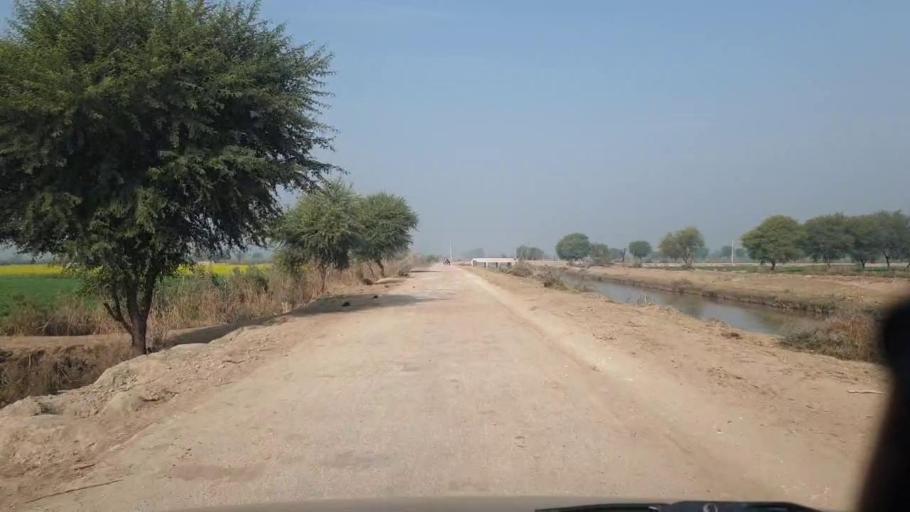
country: PK
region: Sindh
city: Shahdadpur
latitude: 26.0383
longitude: 68.5292
